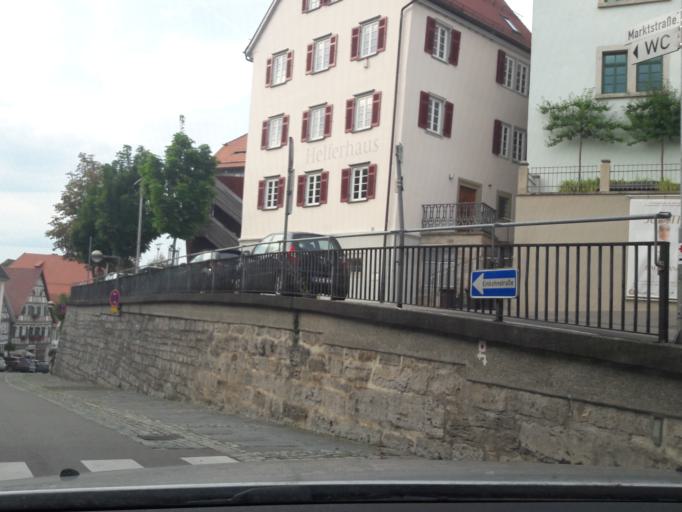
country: DE
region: Baden-Wuerttemberg
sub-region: Regierungsbezirk Stuttgart
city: Backnang
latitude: 48.9457
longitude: 9.4316
